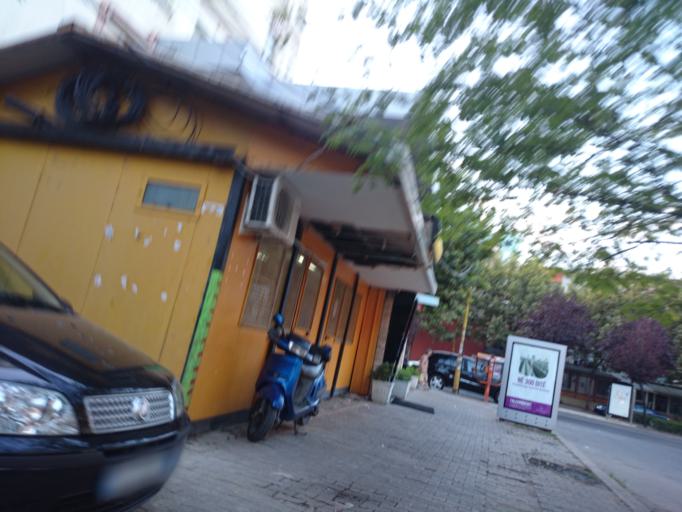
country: AL
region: Tirane
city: Tirana
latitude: 41.3278
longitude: 19.8086
